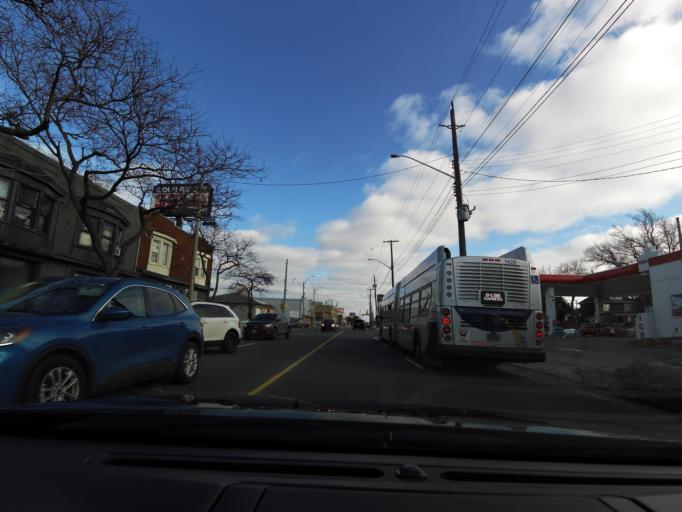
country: CA
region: Ontario
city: Hamilton
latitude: 43.2408
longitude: -79.8117
